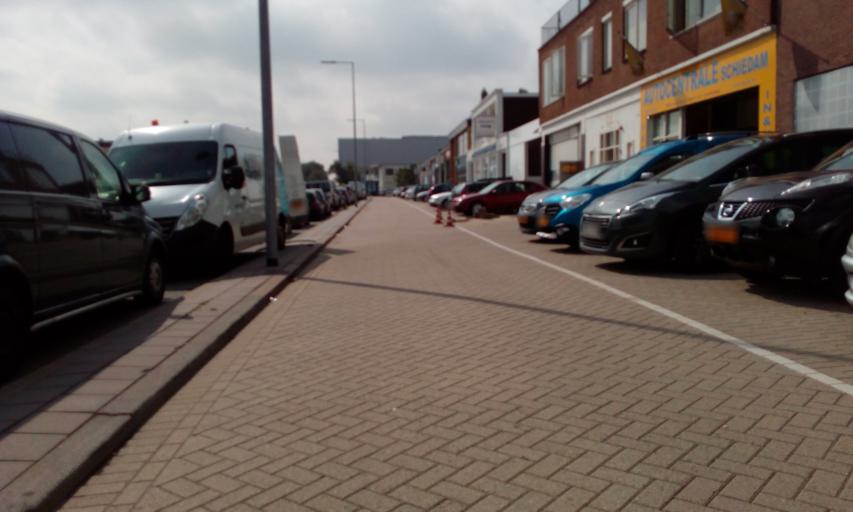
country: NL
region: South Holland
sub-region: Gemeente Schiedam
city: Schiedam
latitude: 51.9117
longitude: 4.4090
